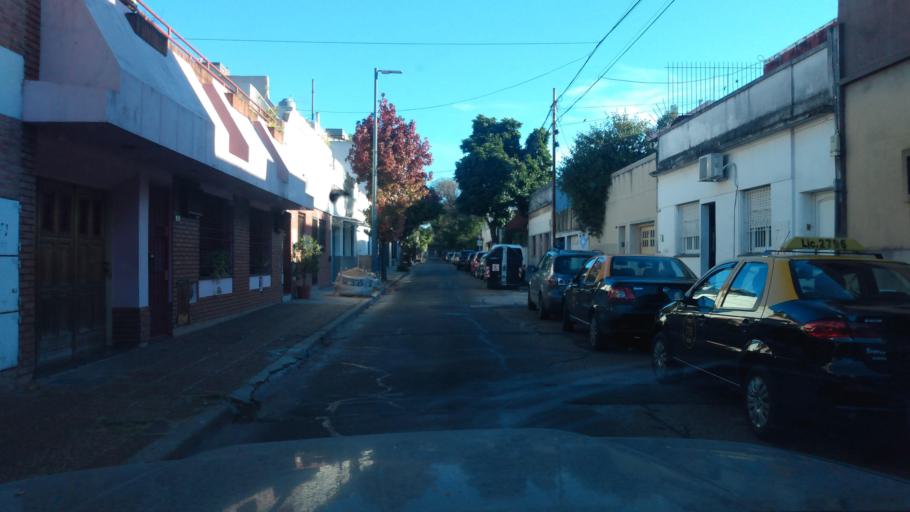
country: AR
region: Buenos Aires F.D.
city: Villa Santa Rita
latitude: -34.5870
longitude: -58.4831
